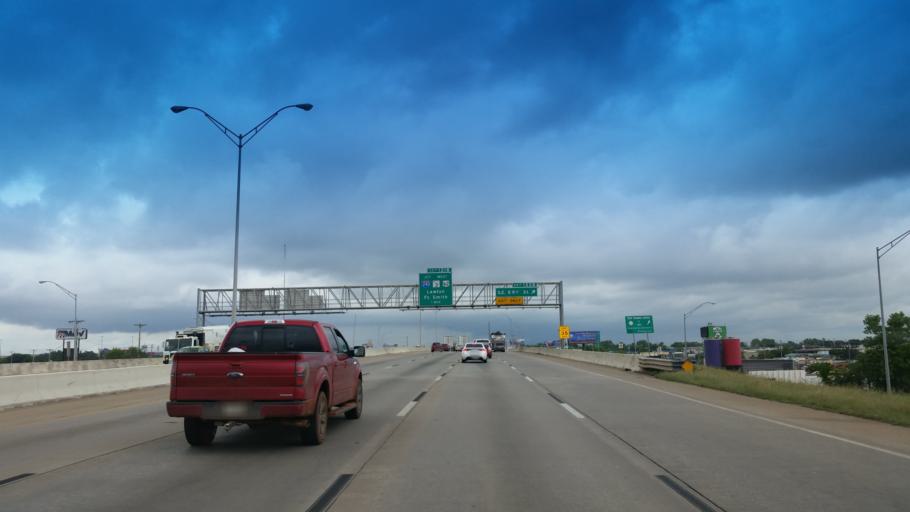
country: US
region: Oklahoma
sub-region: Oklahoma County
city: Del City
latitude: 35.4106
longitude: -97.4925
